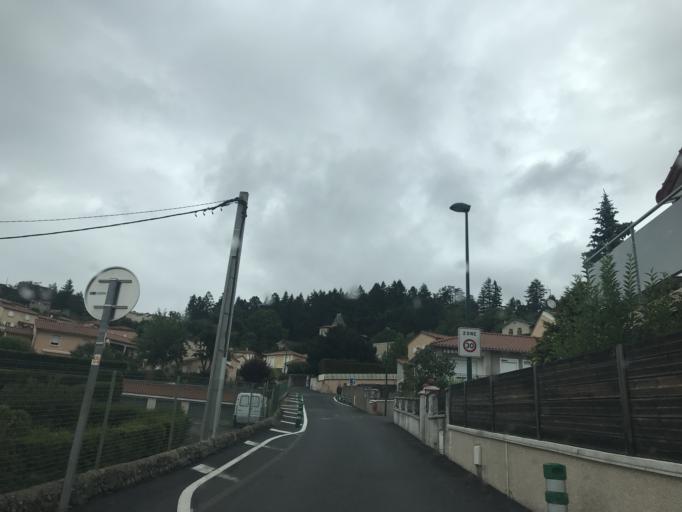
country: FR
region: Auvergne
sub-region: Departement de la Haute-Loire
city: Le Puy-en-Velay
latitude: 45.0541
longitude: 3.8802
